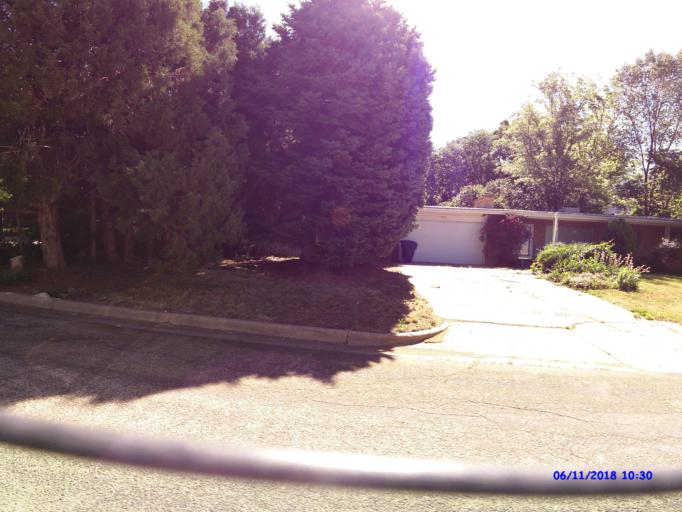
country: US
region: Utah
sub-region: Weber County
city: Ogden
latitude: 41.2302
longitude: -111.9423
